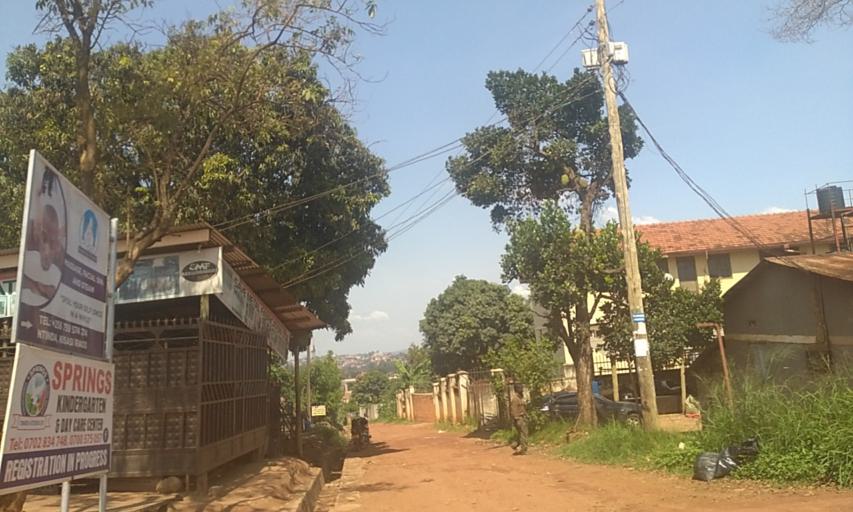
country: UG
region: Central Region
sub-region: Wakiso District
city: Kireka
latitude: 0.3625
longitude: 32.6071
